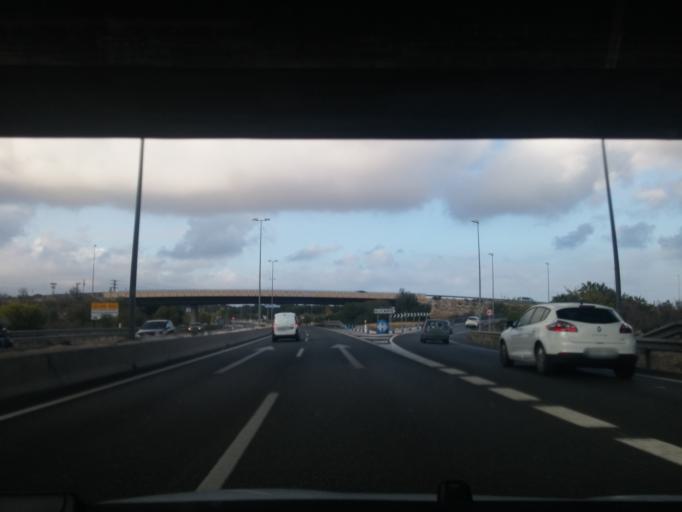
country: ES
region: Valencia
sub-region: Provincia de Alicante
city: San Juan de Alicante
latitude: 38.3815
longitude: -0.4597
